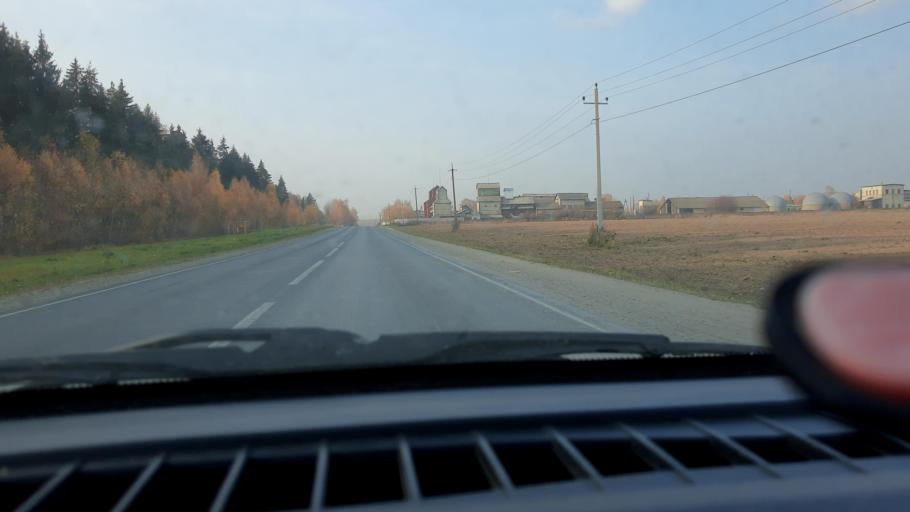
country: RU
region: Nizjnij Novgorod
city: Gorodets
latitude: 56.6335
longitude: 43.5323
